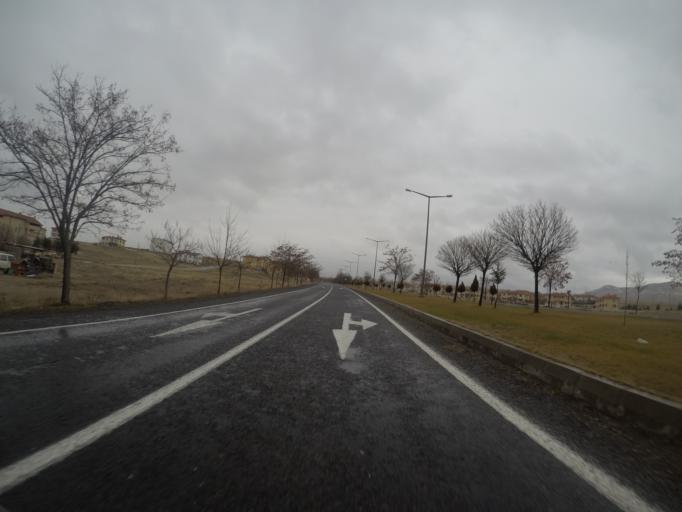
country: TR
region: Nevsehir
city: Avanos
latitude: 38.7010
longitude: 34.8611
